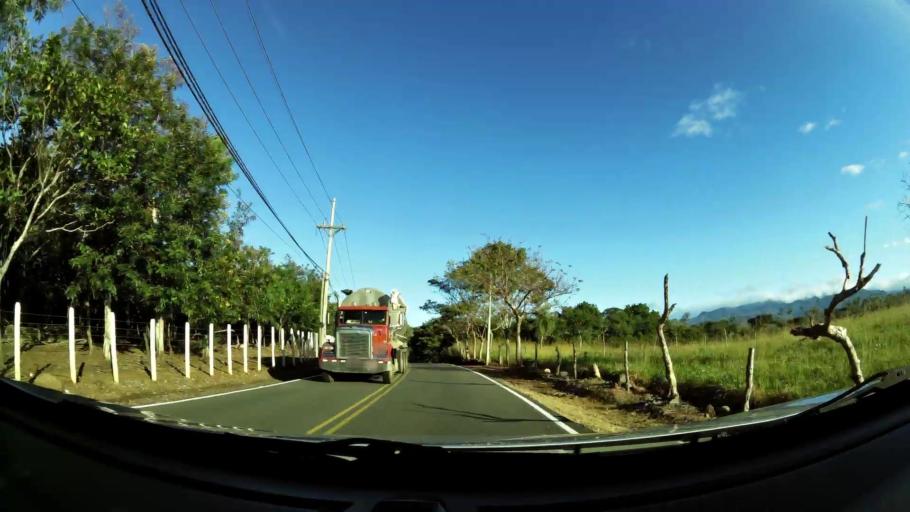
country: CR
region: Puntarenas
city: Miramar
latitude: 10.1018
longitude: -84.8222
